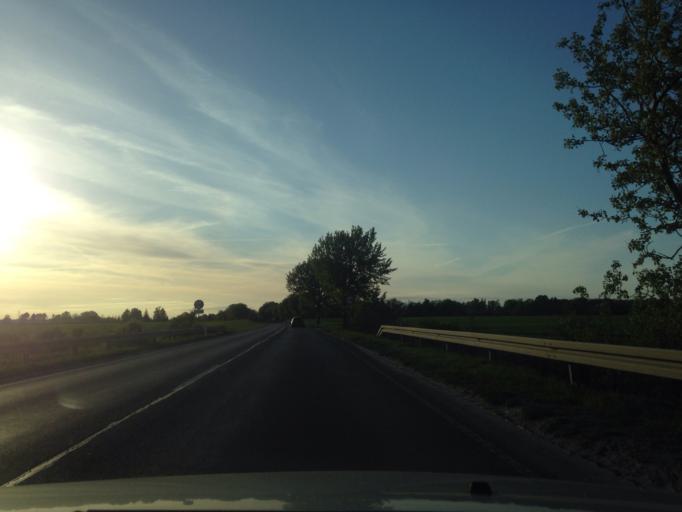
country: DK
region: Zealand
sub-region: Greve Kommune
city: Tune
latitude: 55.5945
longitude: 12.2361
